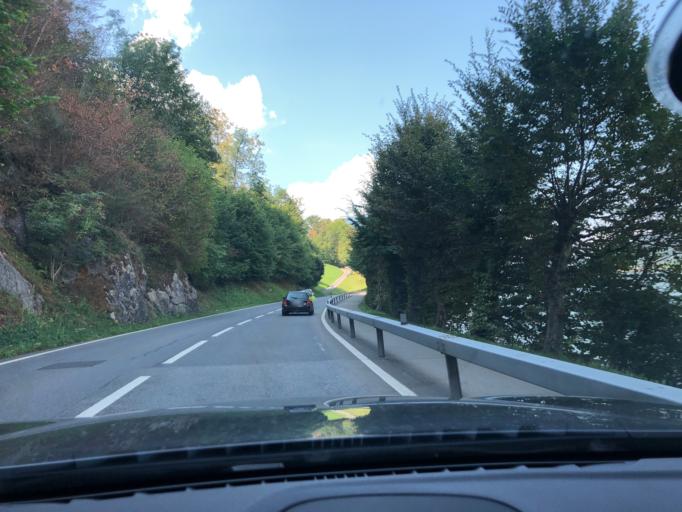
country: CH
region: Schwyz
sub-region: Bezirk Schwyz
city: Steinen
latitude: 47.0303
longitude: 8.5996
